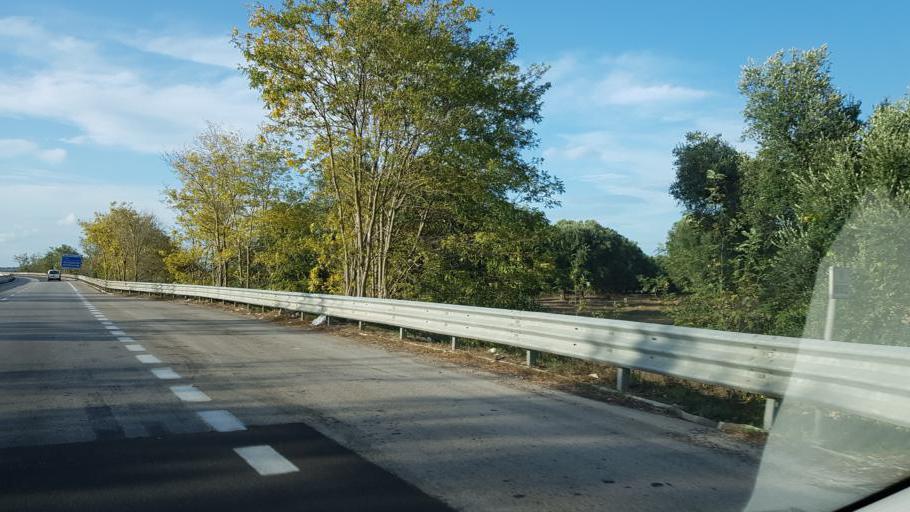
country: IT
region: Apulia
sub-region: Provincia di Brindisi
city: Francavilla Fontana
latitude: 40.5438
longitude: 17.5987
